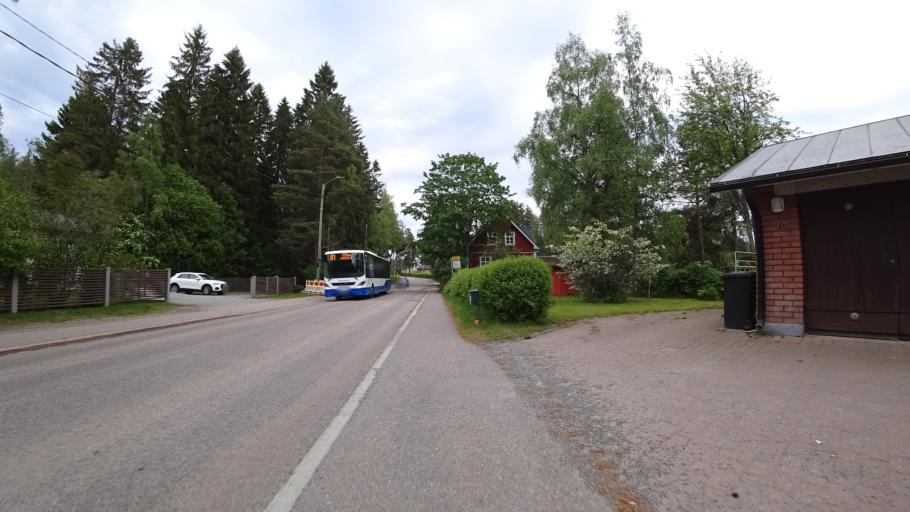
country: FI
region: Pirkanmaa
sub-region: Tampere
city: Yloejaervi
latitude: 61.5242
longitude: 23.6265
